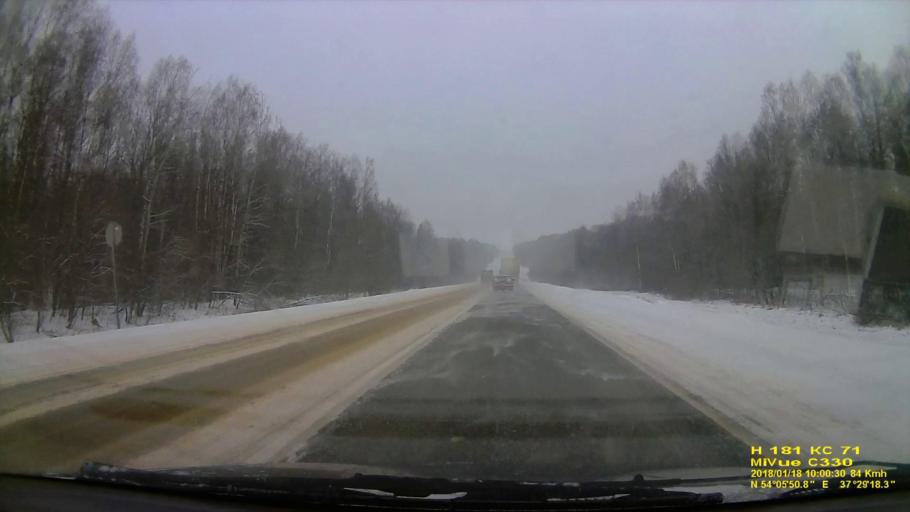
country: RU
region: Tula
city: Pervomayskiy
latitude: 54.0973
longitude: 37.4884
